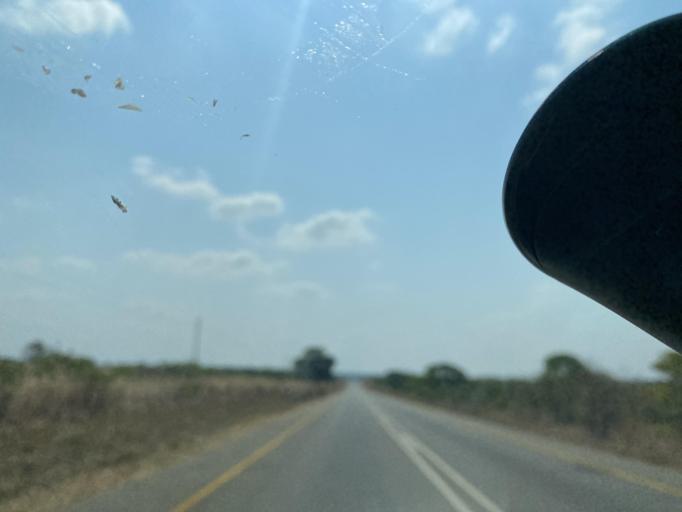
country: ZM
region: Lusaka
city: Chongwe
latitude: -15.5304
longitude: 28.6304
